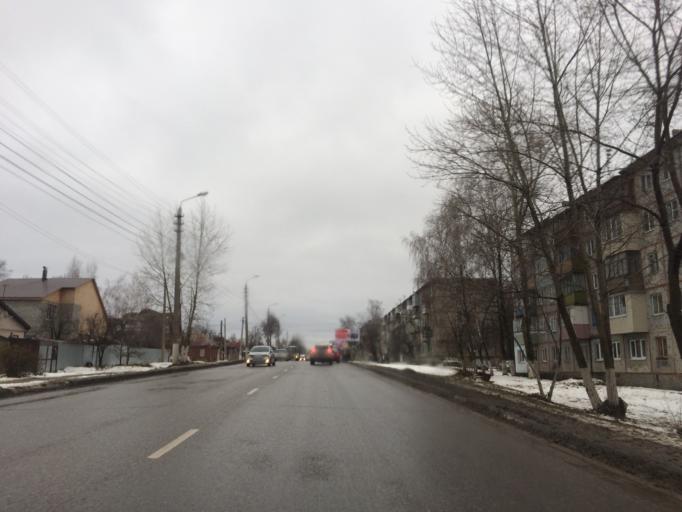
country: RU
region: Tula
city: Tula
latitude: 54.1991
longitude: 37.6856
